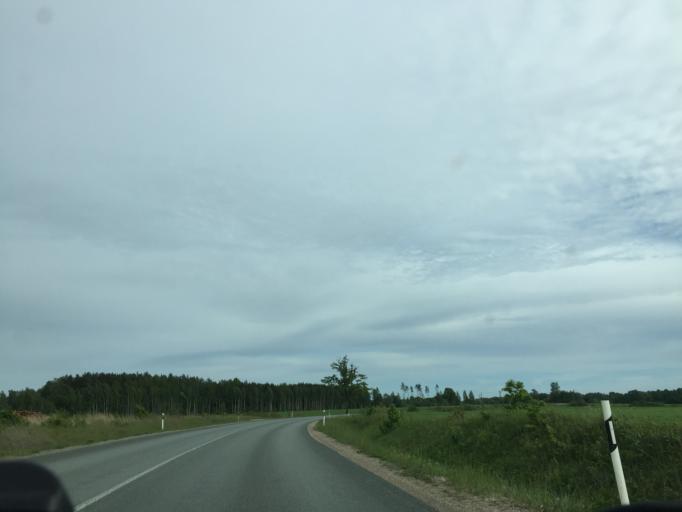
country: LV
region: Beverina
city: Murmuiza
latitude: 57.4661
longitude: 25.4135
